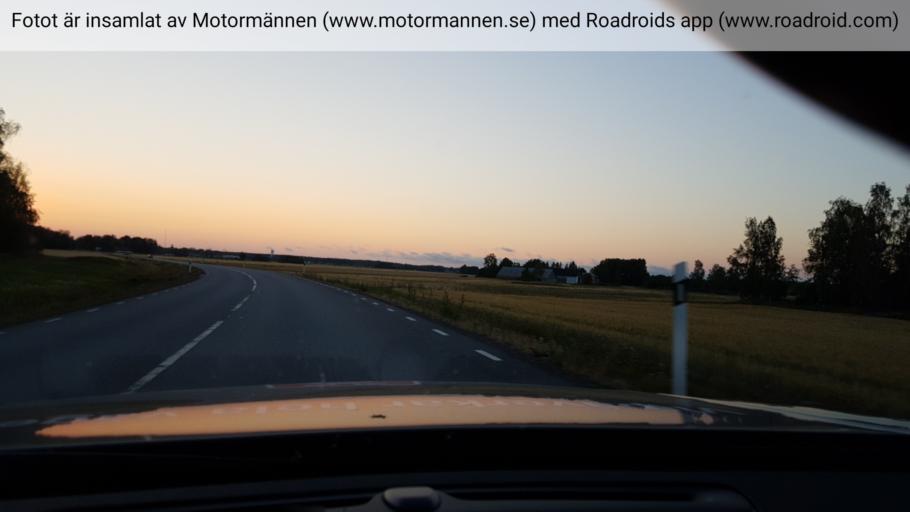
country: SE
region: Uppsala
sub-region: Heby Kommun
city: OEstervala
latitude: 60.1601
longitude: 17.2048
